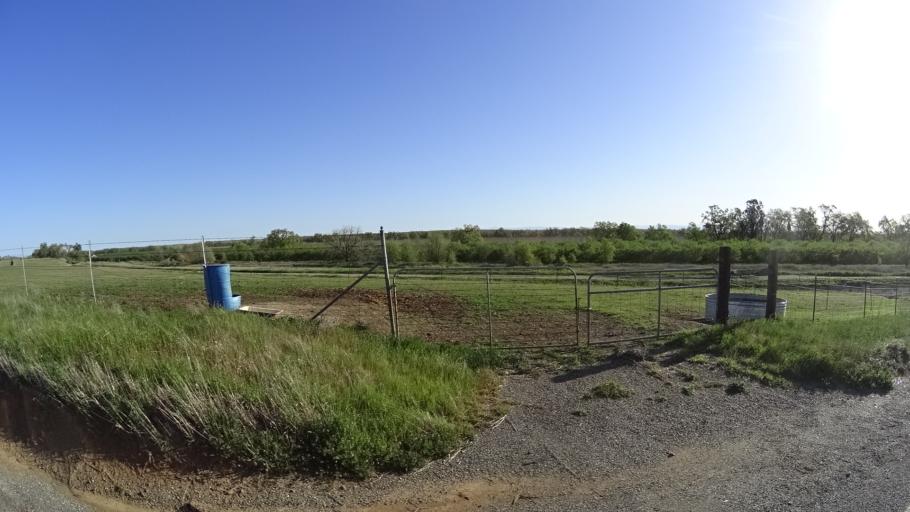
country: US
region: California
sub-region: Glenn County
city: Orland
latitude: 39.7994
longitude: -122.3213
